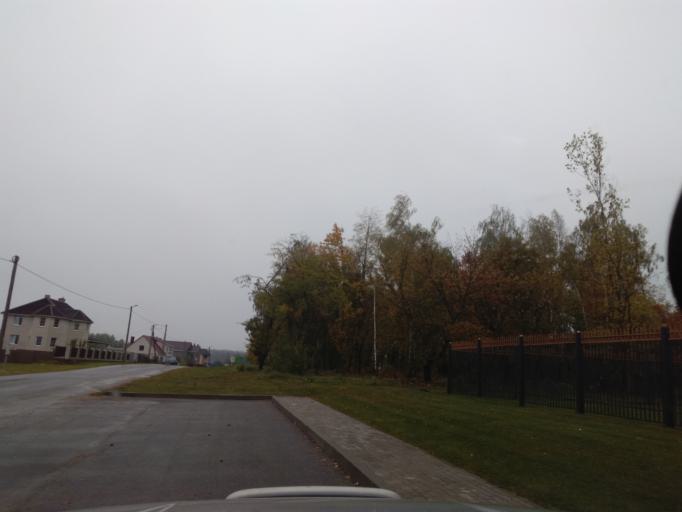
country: BY
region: Minsk
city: Kapyl'
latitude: 53.1552
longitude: 27.0966
